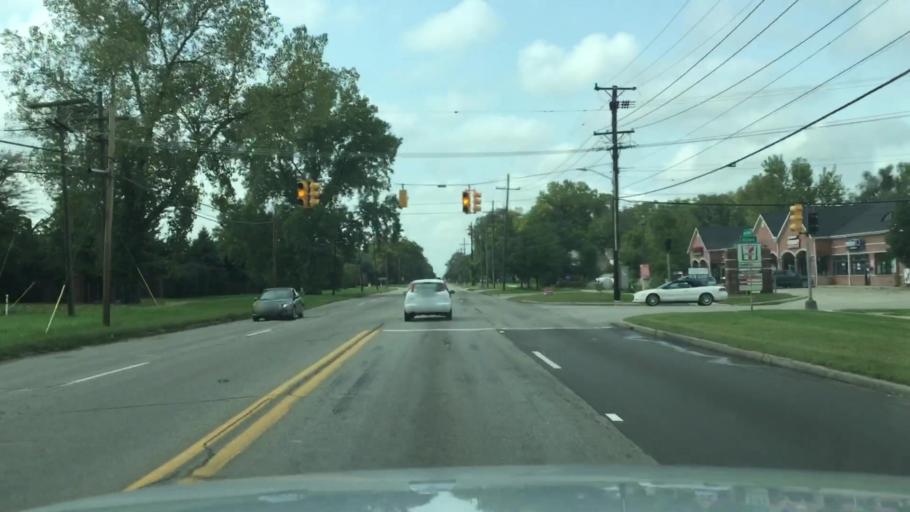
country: US
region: Michigan
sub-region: Wayne County
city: Wayne
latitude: 42.2670
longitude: -83.3717
